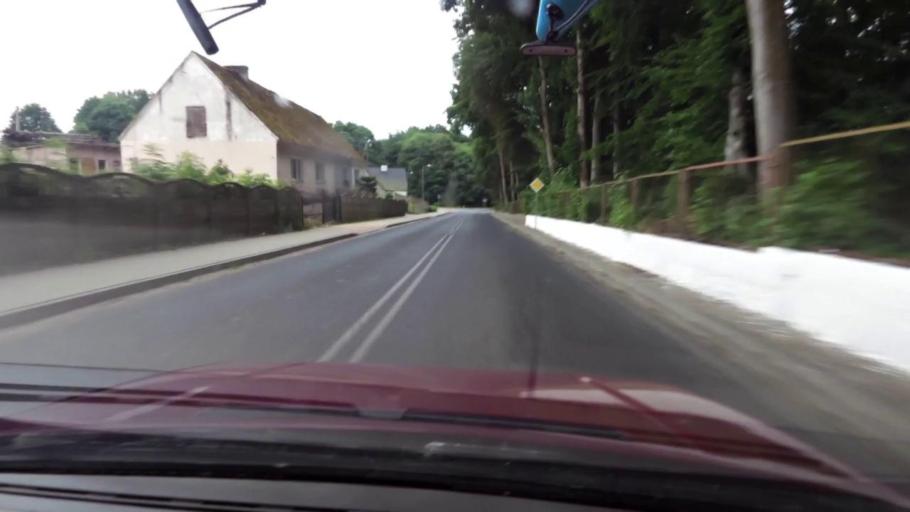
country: PL
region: West Pomeranian Voivodeship
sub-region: Powiat koszalinski
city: Polanow
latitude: 54.1391
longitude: 16.5225
